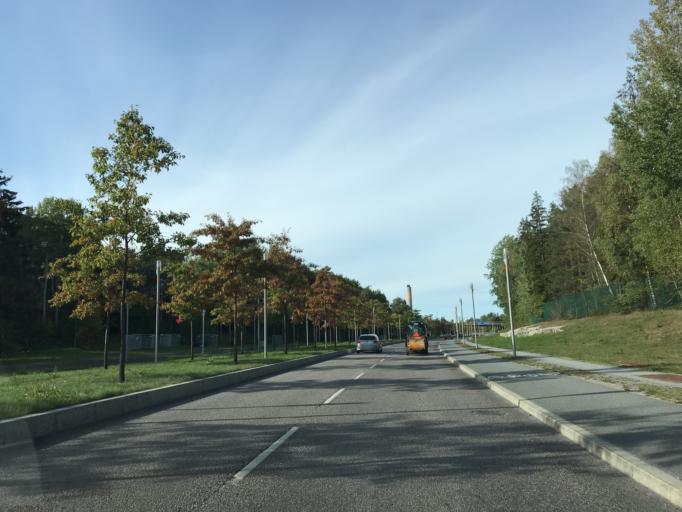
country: SE
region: Stockholm
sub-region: Stockholms Kommun
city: Kista
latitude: 59.4096
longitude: 17.9350
